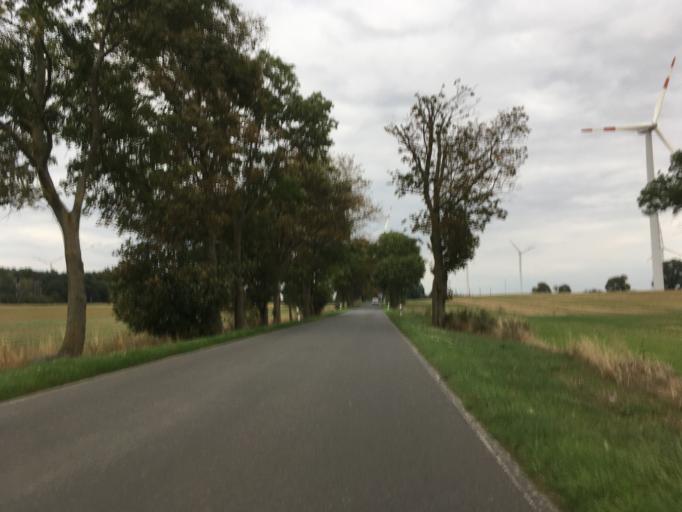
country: DE
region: Brandenburg
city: Passow
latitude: 53.0905
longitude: 14.1661
